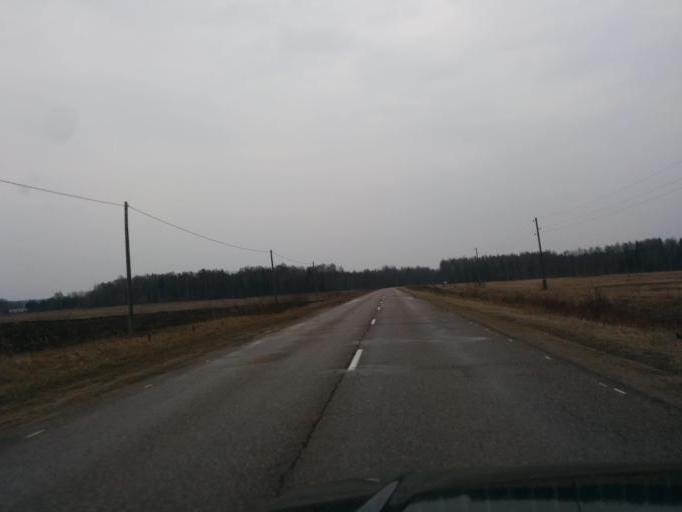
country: LV
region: Ikskile
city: Ikskile
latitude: 56.8188
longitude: 24.4580
